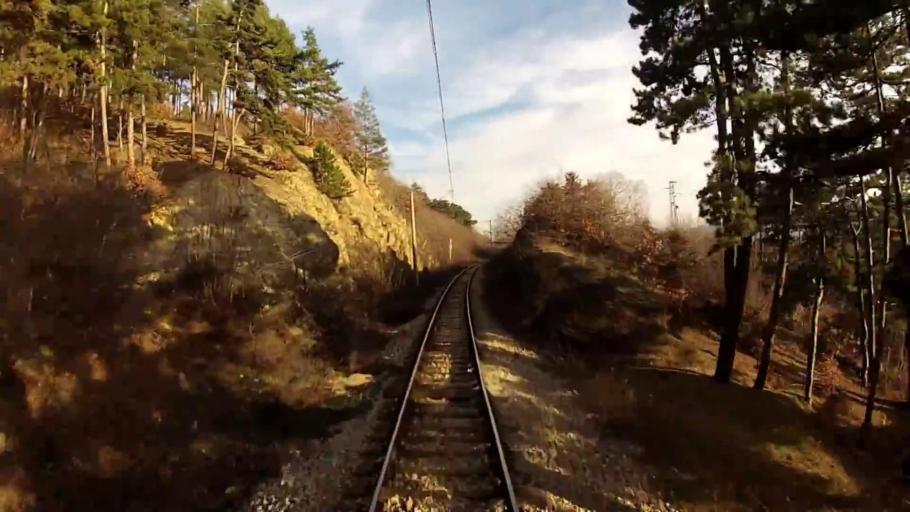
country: BG
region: Plovdiv
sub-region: Obshtina Karlovo
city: Klisura
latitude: 42.7193
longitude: 24.5974
